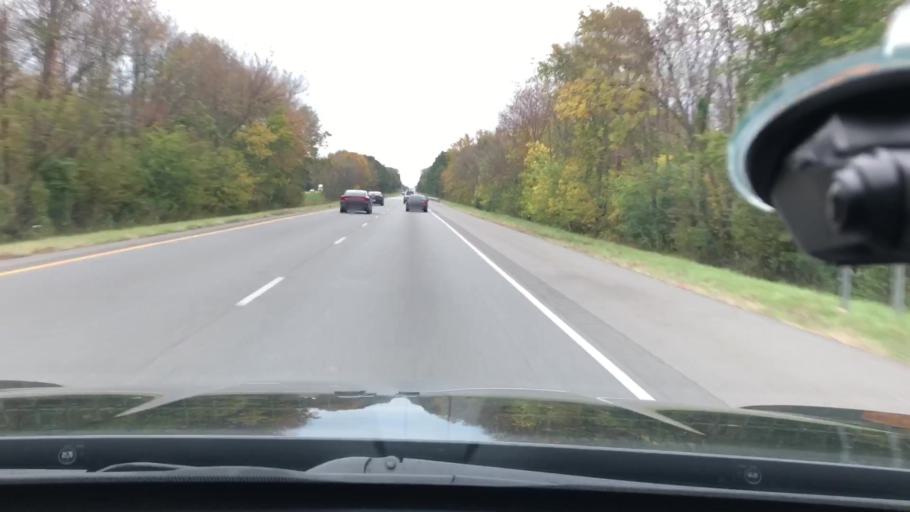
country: US
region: Arkansas
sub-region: Hempstead County
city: Hope
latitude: 33.6345
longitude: -93.7131
